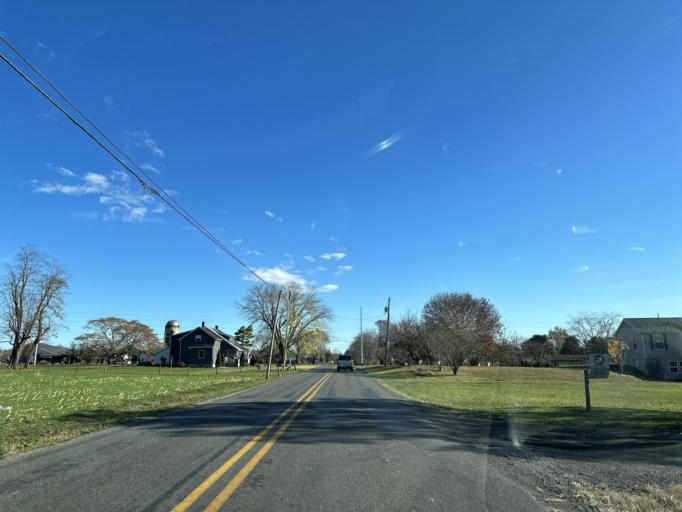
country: US
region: Virginia
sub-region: Rockingham County
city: Bridgewater
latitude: 38.4632
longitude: -79.0195
